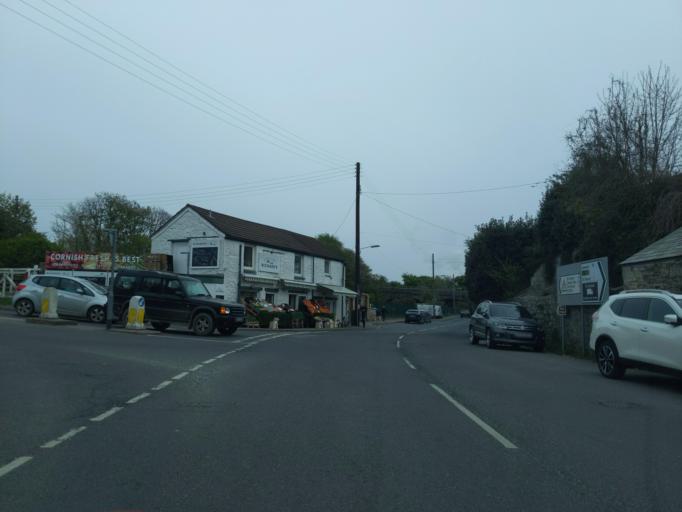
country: GB
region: England
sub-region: Cornwall
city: Par
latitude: 50.3501
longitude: -4.7079
